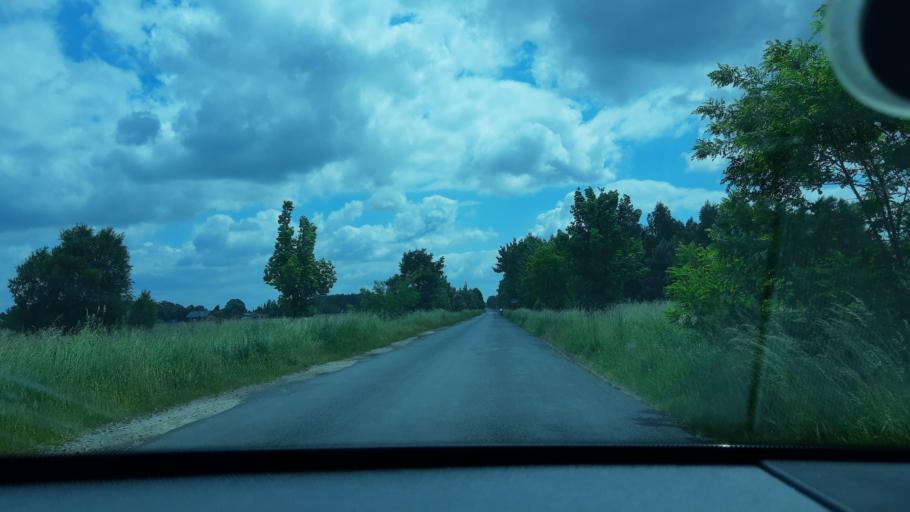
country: PL
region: Lodz Voivodeship
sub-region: Powiat sieradzki
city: Sieradz
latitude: 51.5431
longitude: 18.7911
